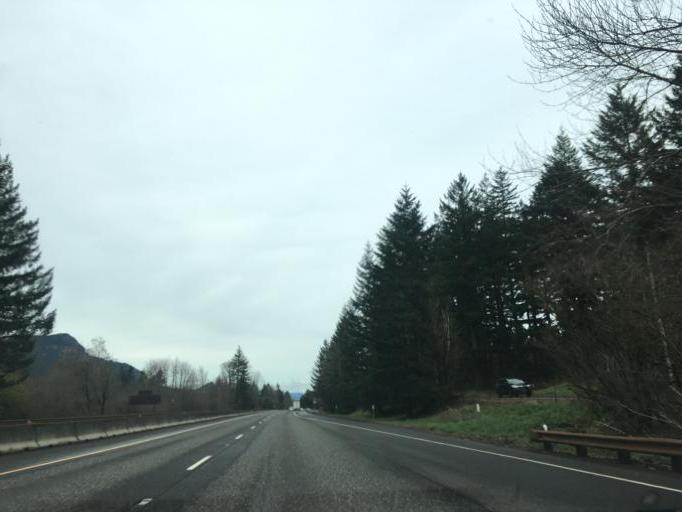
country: US
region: Oregon
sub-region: Hood River County
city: Cascade Locks
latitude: 45.6040
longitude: -122.0399
